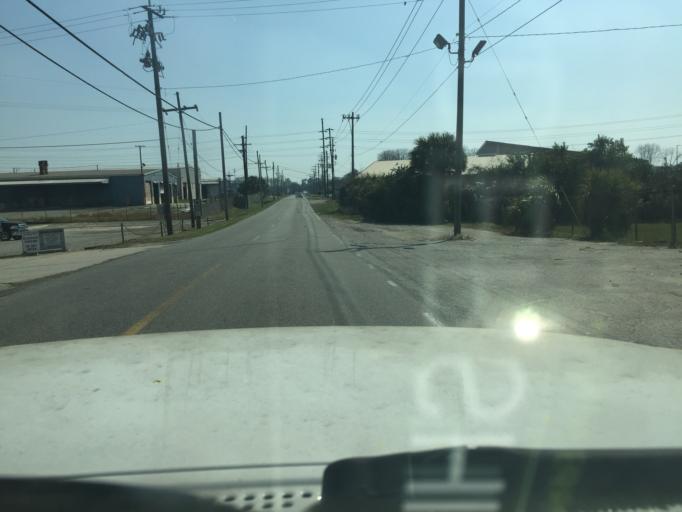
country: US
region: Georgia
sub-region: Chatham County
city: Savannah
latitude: 32.0912
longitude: -81.1111
